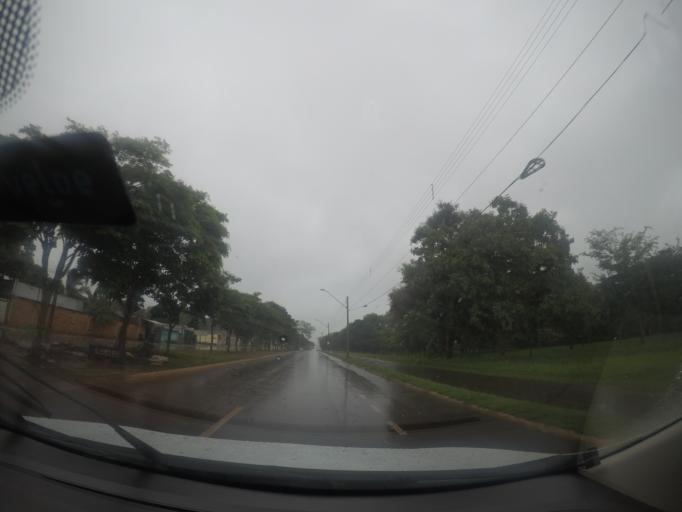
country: BR
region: Goias
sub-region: Goiania
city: Goiania
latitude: -16.5999
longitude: -49.3397
